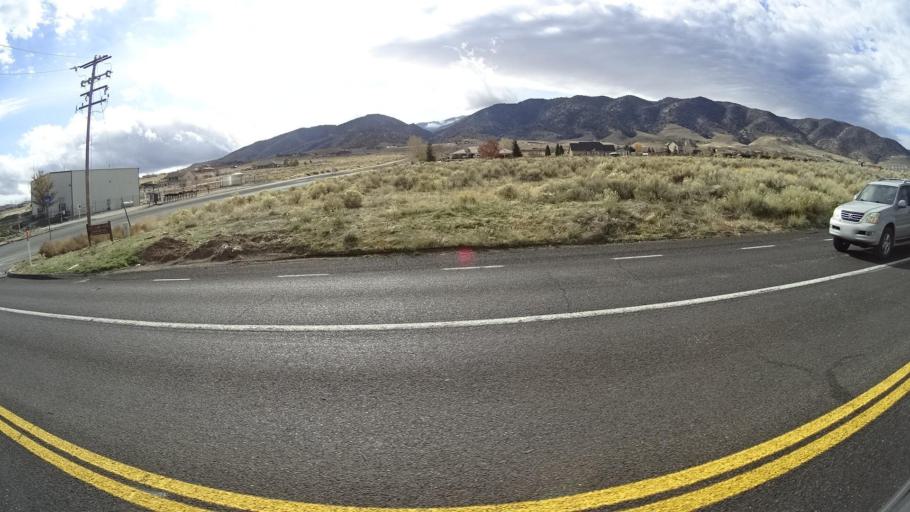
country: US
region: California
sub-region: Kern County
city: Tehachapi
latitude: 35.1110
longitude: -118.4482
